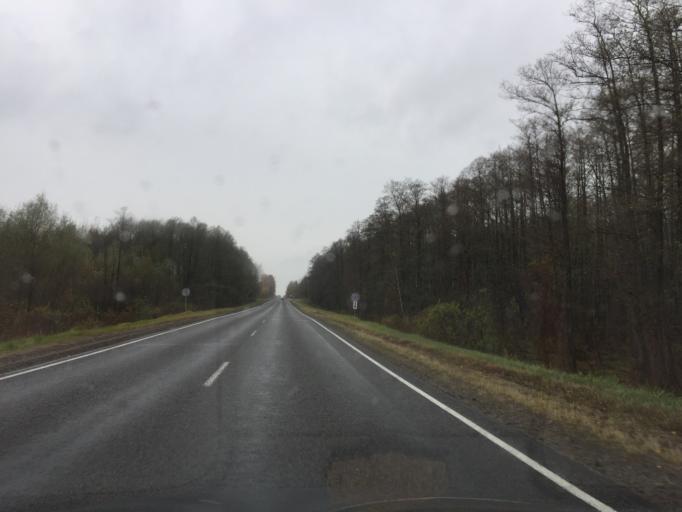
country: BY
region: Mogilev
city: Slawharad
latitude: 53.3506
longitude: 30.8220
